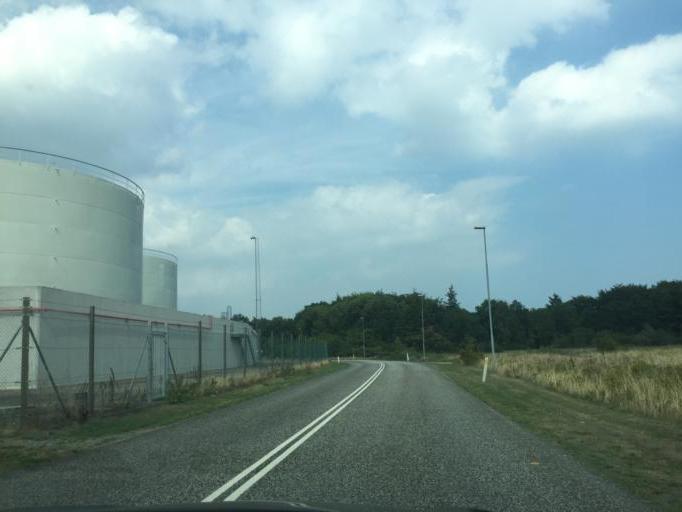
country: DK
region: South Denmark
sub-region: Nyborg Kommune
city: Nyborg
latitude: 55.2992
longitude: 10.8164
